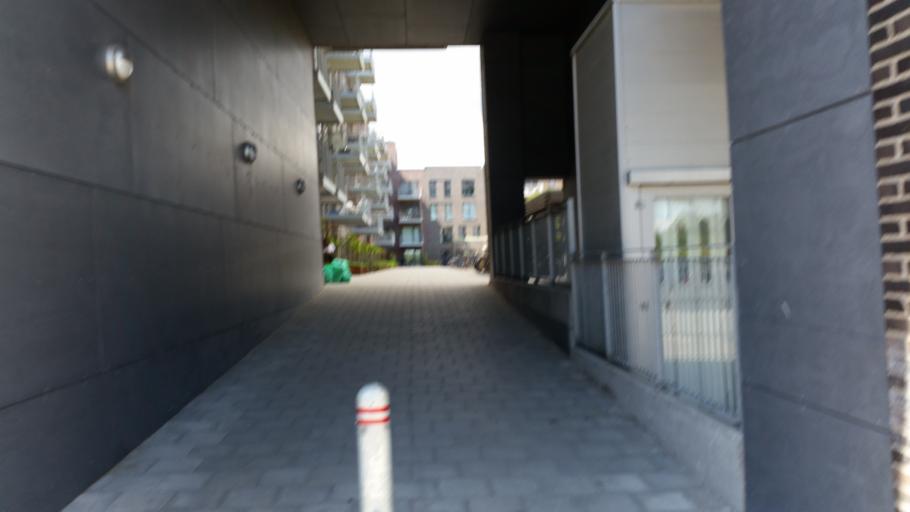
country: DK
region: Capital Region
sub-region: Kobenhavn
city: Copenhagen
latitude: 55.6489
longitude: 12.5546
